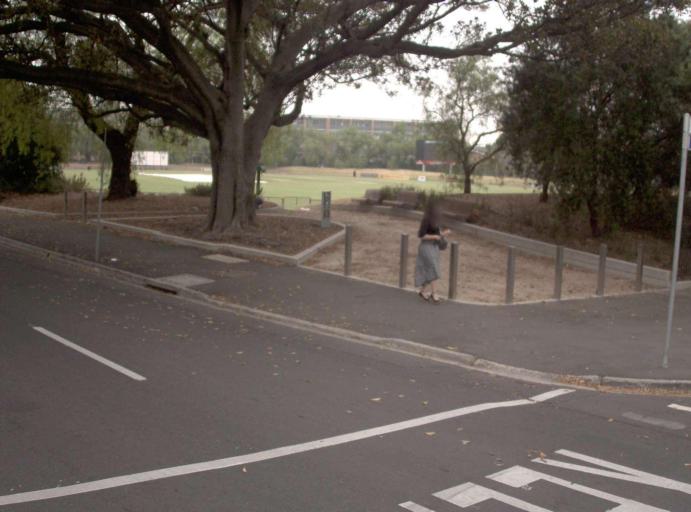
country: AU
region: Victoria
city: Toorak
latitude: -37.8535
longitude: 145.0117
